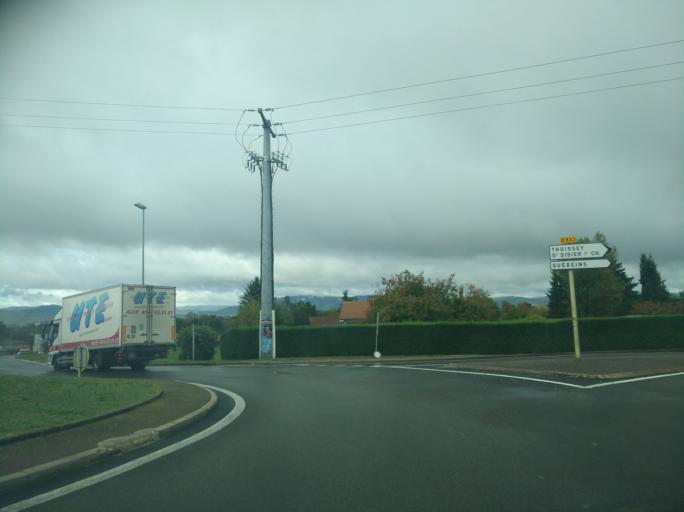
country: FR
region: Rhone-Alpes
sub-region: Departement de l'Ain
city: Guereins
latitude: 46.1001
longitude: 4.7748
